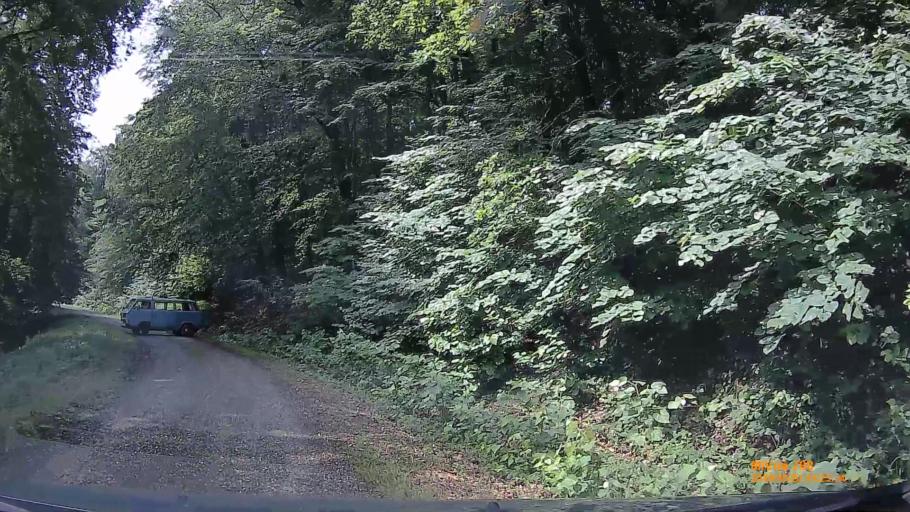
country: HU
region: Baranya
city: Mecseknadasd
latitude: 46.2103
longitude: 18.4858
